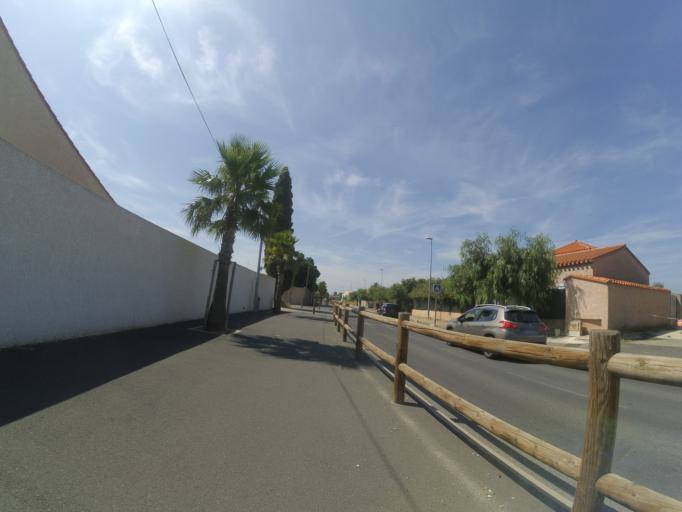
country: FR
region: Languedoc-Roussillon
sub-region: Departement des Pyrenees-Orientales
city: Rivesaltes
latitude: 42.7776
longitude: 2.8746
